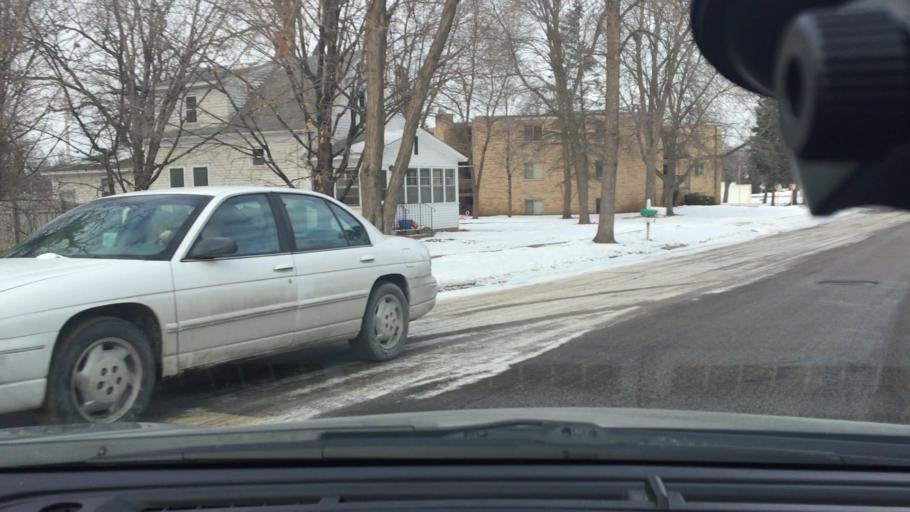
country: US
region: Minnesota
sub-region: Hennepin County
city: Champlin
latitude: 45.1879
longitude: -93.3985
